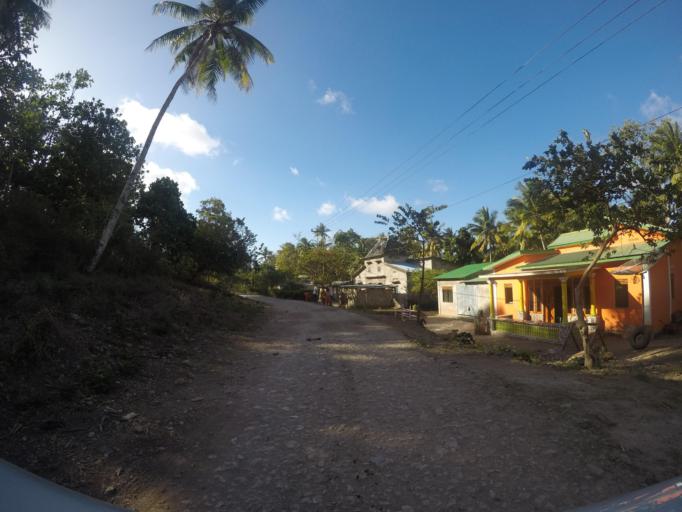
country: TL
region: Lautem
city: Lospalos
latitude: -8.4500
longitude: 126.8817
